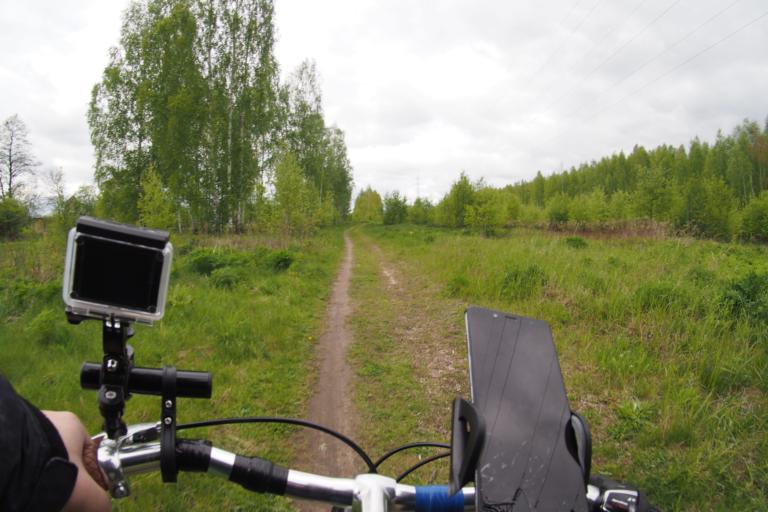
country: RU
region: Moskovskaya
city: Rechitsy
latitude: 55.5546
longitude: 38.4818
